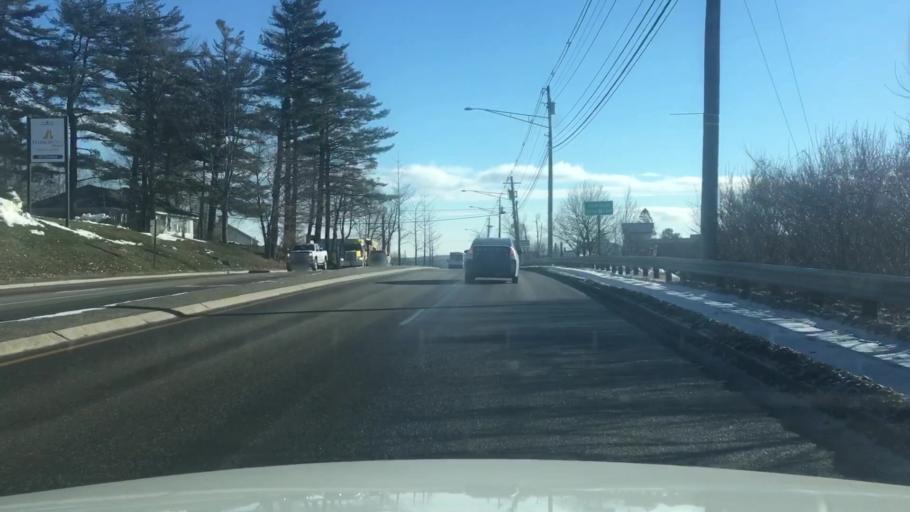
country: US
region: Maine
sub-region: Kennebec County
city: Augusta
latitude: 44.3128
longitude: -69.7935
